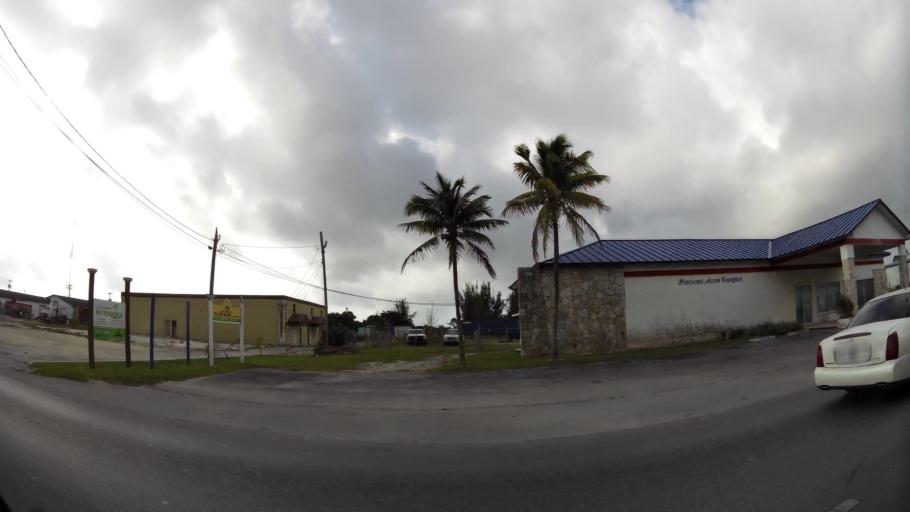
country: BS
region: Freeport
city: Freeport
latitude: 26.5424
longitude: -78.7038
